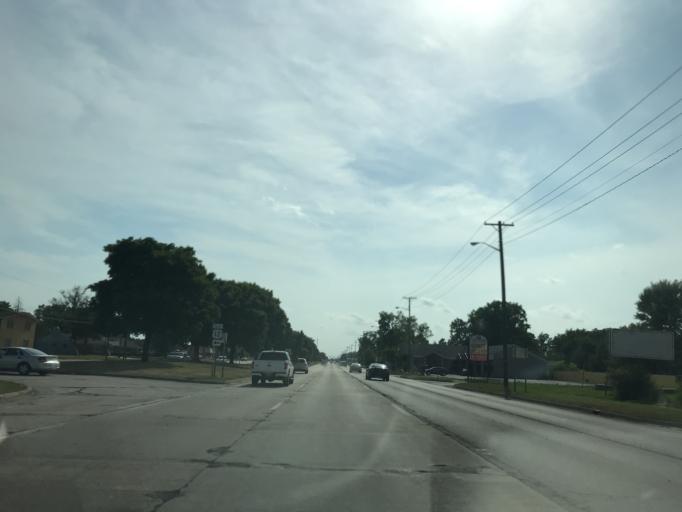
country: US
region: Michigan
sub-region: Wayne County
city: Inkster
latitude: 42.2918
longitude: -83.3207
